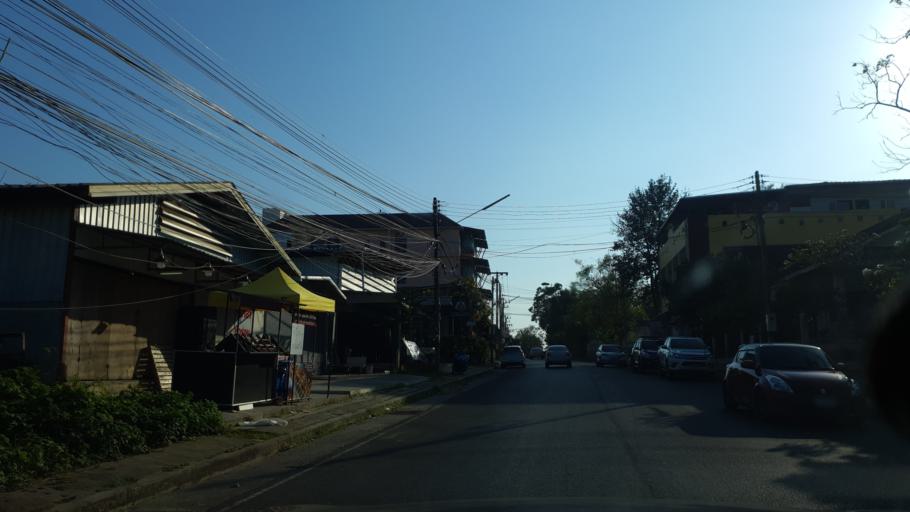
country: TH
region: Krabi
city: Krabi
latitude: 8.0778
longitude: 98.9105
